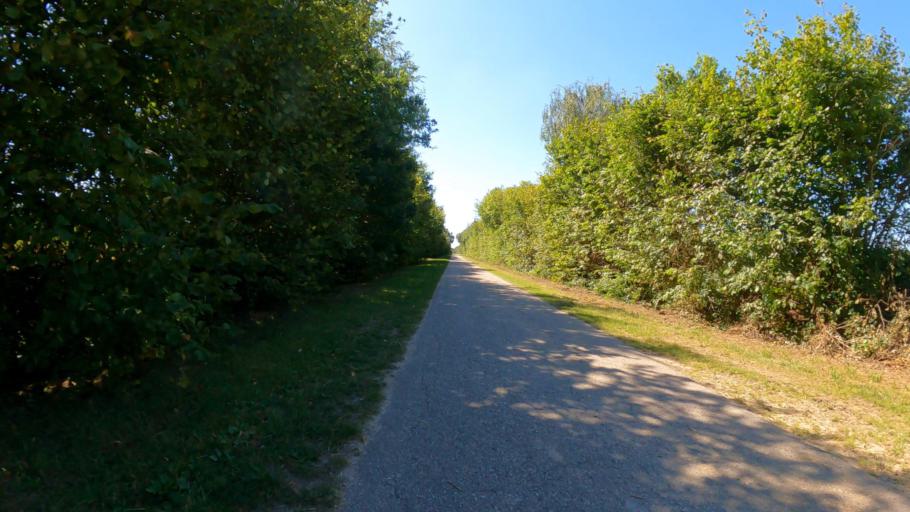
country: DE
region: Schleswig-Holstein
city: Hohenhorn
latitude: 53.4742
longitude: 10.3513
